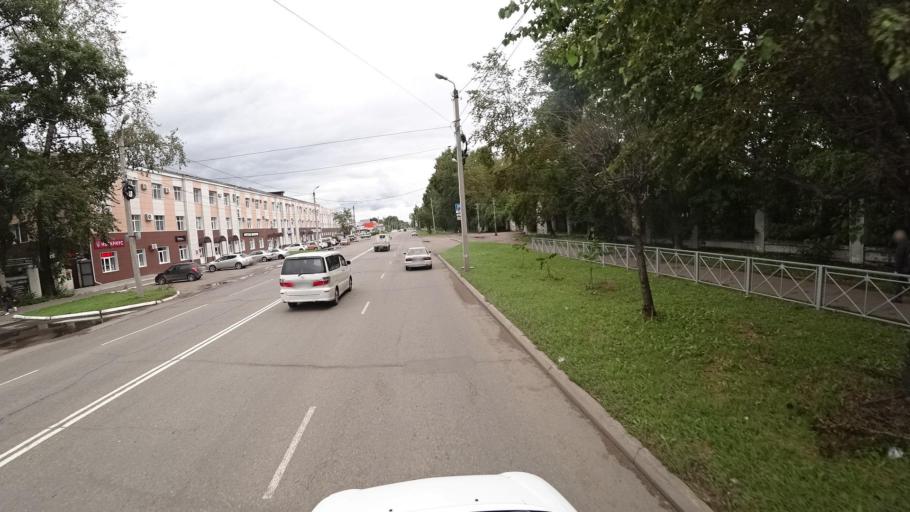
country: RU
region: Khabarovsk Krai
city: Komsomolsk-on-Amur
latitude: 50.5570
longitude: 137.0250
